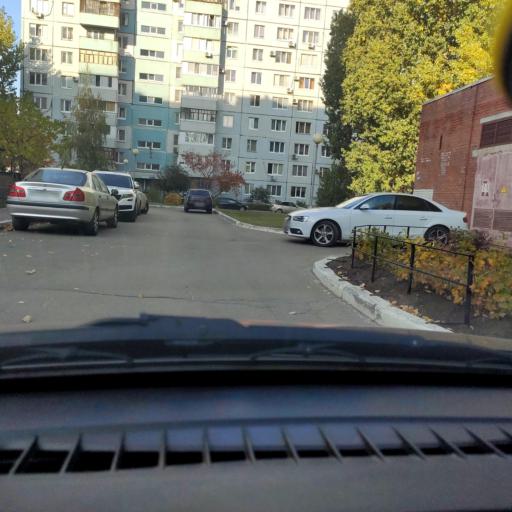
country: RU
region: Samara
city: Tol'yatti
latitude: 53.5455
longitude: 49.3534
